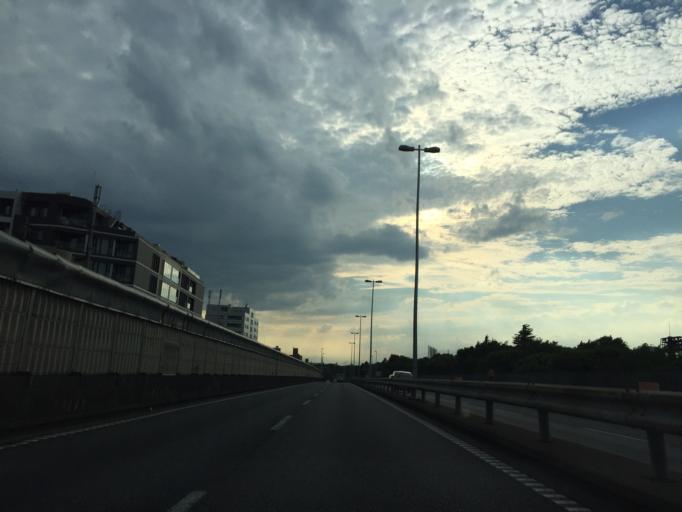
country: JP
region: Tokyo
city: Chofugaoka
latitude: 35.6274
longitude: 139.6256
